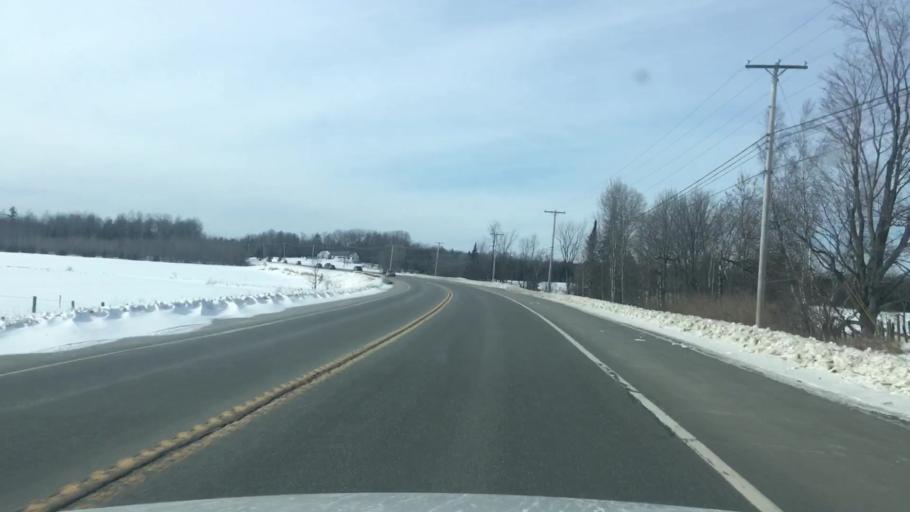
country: US
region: Maine
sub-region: Penobscot County
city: Kenduskeag
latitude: 44.9098
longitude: -68.8971
